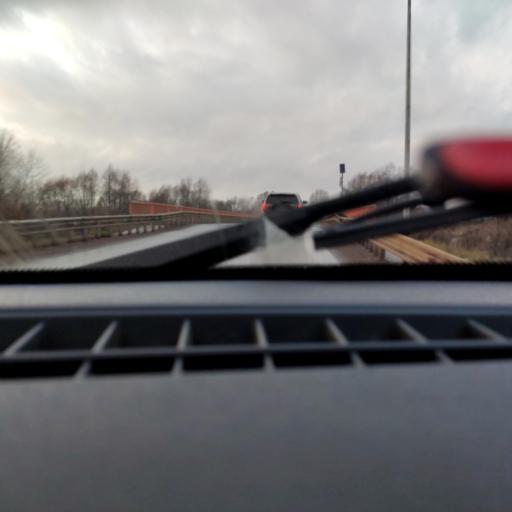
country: RU
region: Bashkortostan
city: Avdon
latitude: 54.5009
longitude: 55.8810
